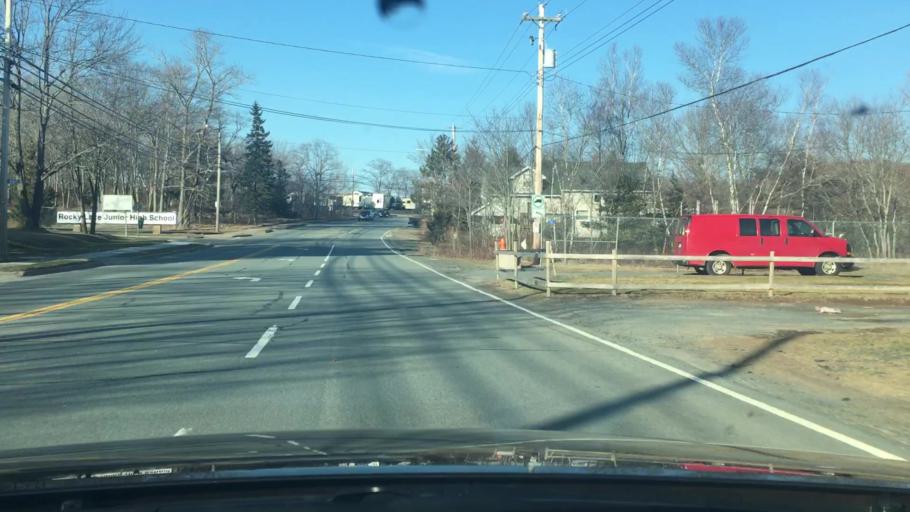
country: CA
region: Nova Scotia
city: Dartmouth
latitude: 44.7448
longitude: -63.6368
